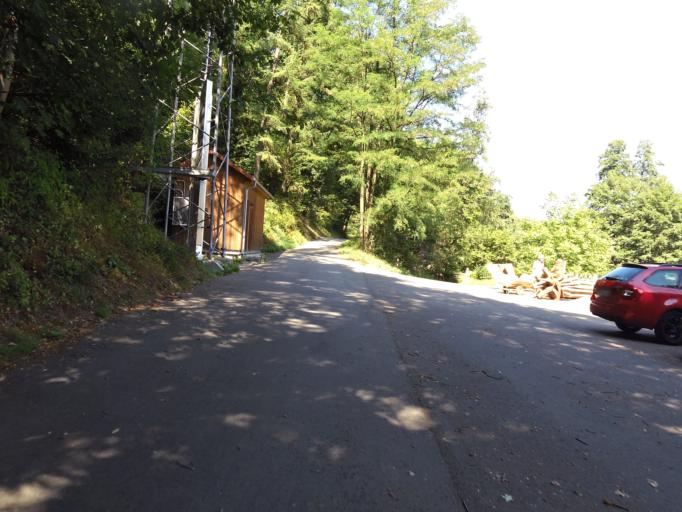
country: DE
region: Baden-Wuerttemberg
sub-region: Karlsruhe Region
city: Neunkirchen
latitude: 49.4187
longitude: 8.9999
